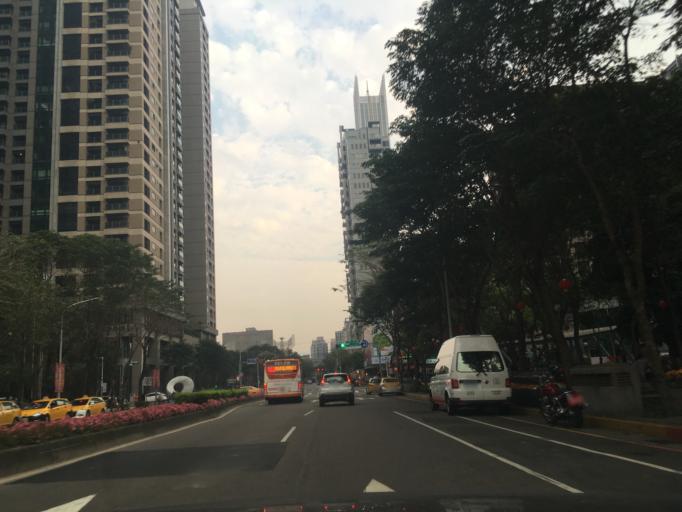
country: TW
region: Taipei
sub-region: Taipei
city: Banqiao
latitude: 25.0132
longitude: 121.4663
